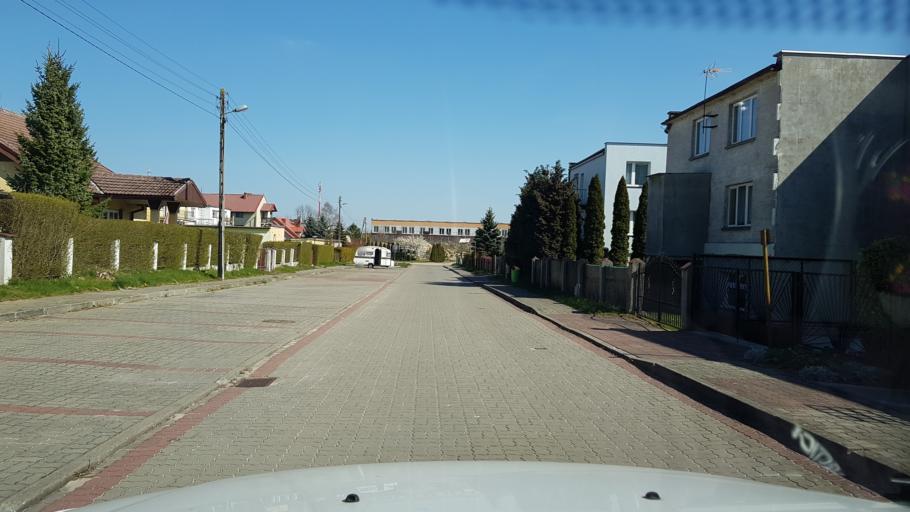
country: PL
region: West Pomeranian Voivodeship
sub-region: Powiat slawienski
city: Darlowo
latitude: 54.5396
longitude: 16.5436
